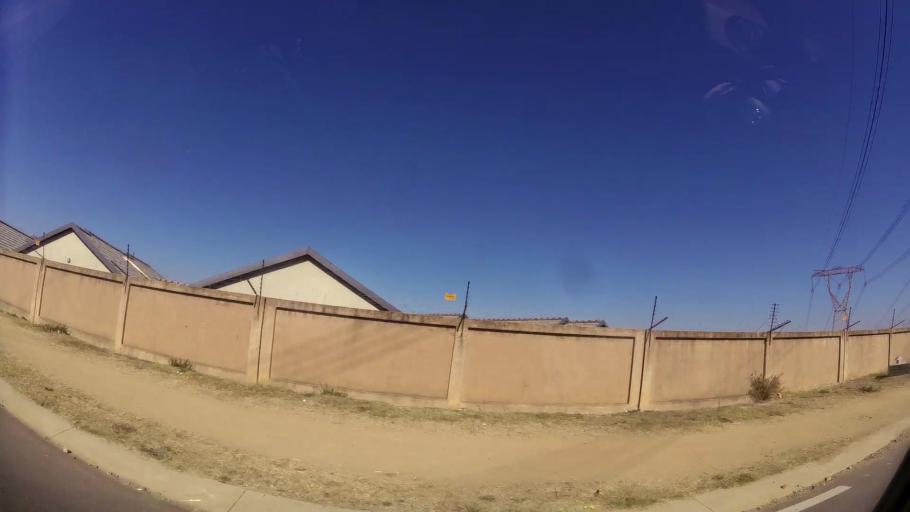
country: ZA
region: Gauteng
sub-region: City of Johannesburg Metropolitan Municipality
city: Midrand
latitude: -25.9122
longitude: 28.1298
